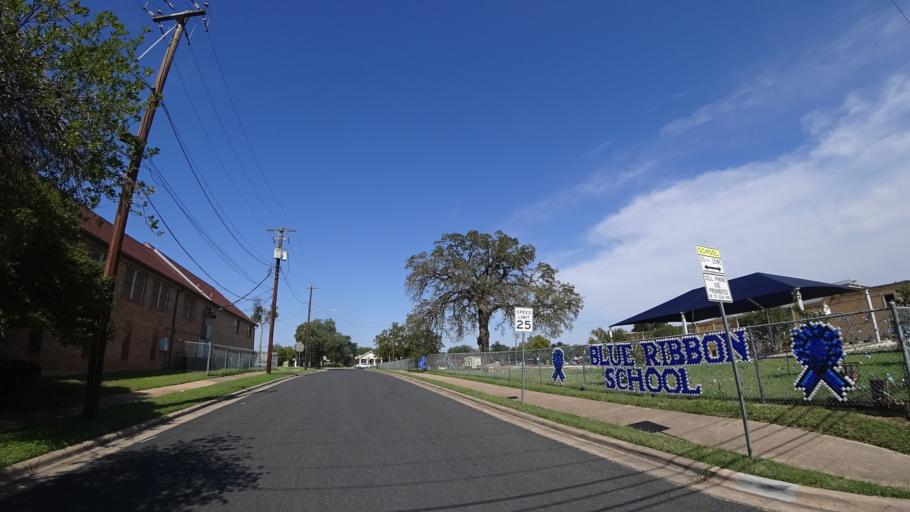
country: US
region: Texas
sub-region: Travis County
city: Austin
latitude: 30.2671
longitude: -97.7234
